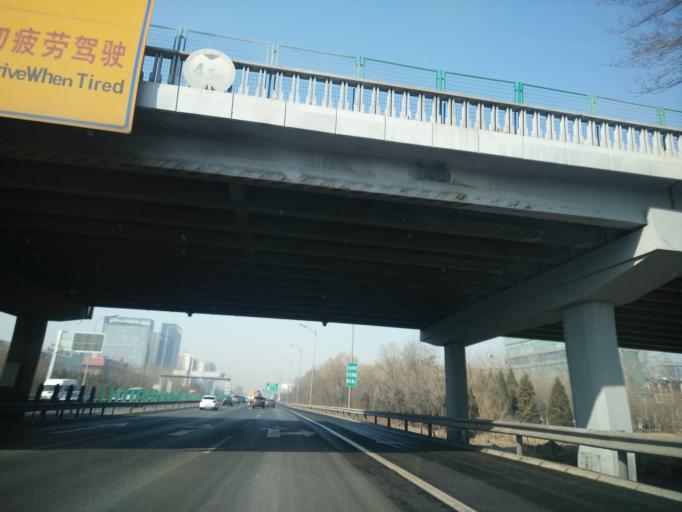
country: CN
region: Beijing
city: Wangjing
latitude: 40.0139
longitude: 116.4722
